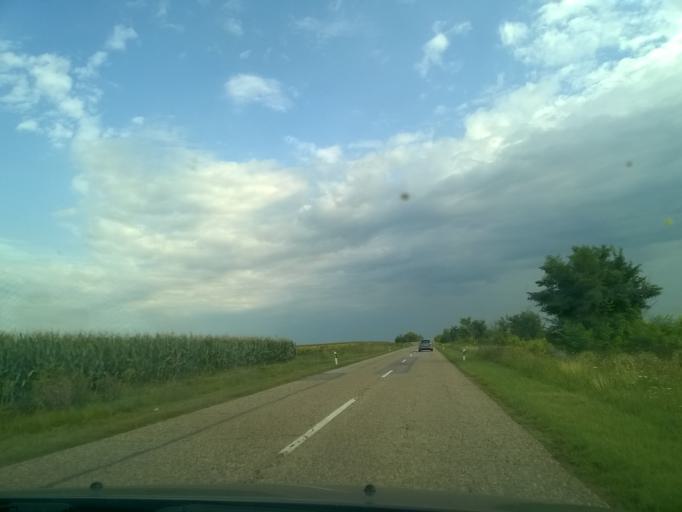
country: RS
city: Uzdin
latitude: 45.1675
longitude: 20.6174
